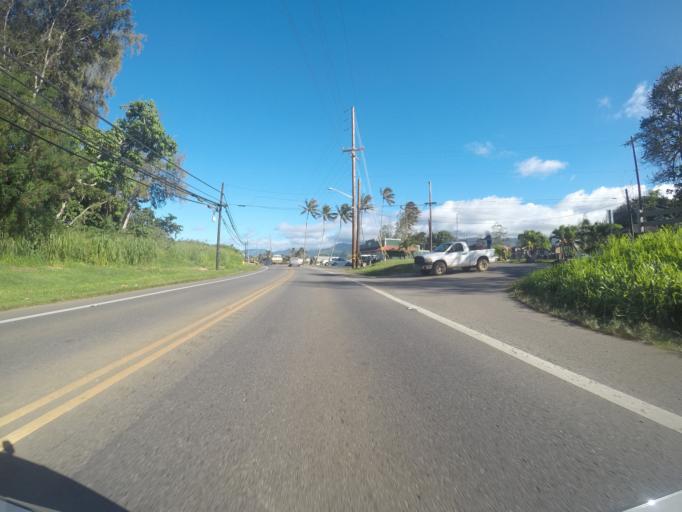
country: US
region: Hawaii
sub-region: Honolulu County
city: La'ie
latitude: 21.6551
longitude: -157.9305
